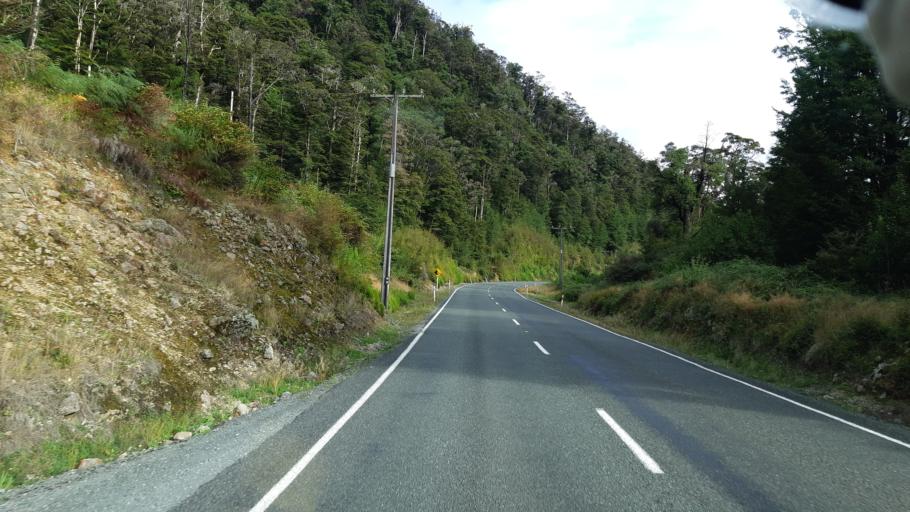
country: NZ
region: West Coast
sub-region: Buller District
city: Westport
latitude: -41.9976
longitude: 172.2243
